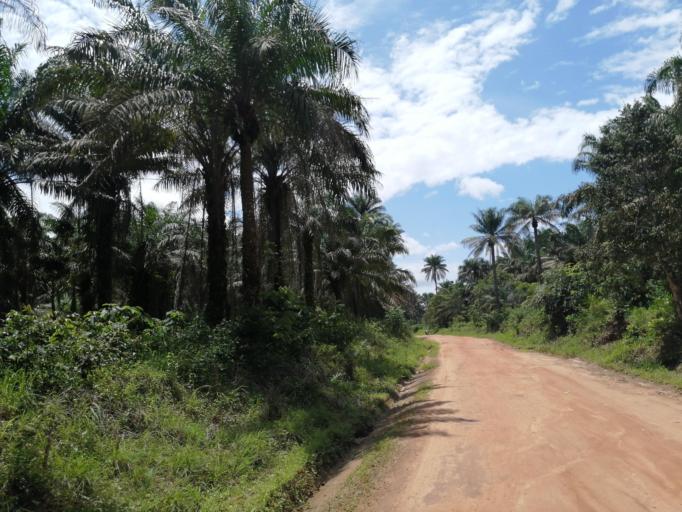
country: SL
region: Northern Province
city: Konakridee
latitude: 8.7590
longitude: -13.1403
